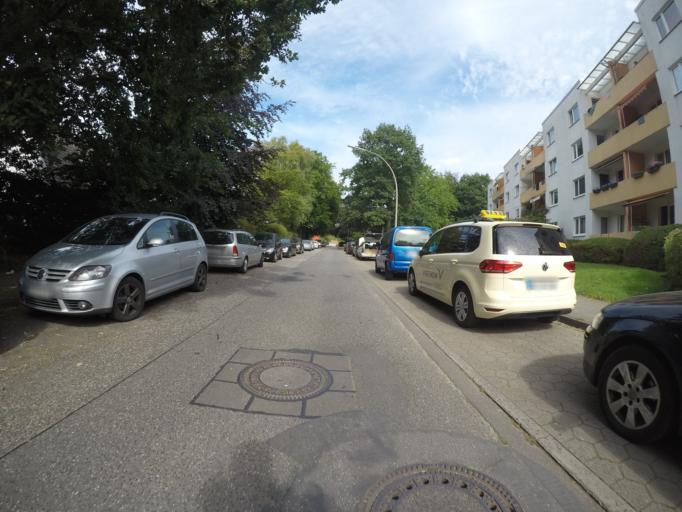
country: DE
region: Hamburg
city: Eidelstedt
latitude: 53.6250
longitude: 9.9134
